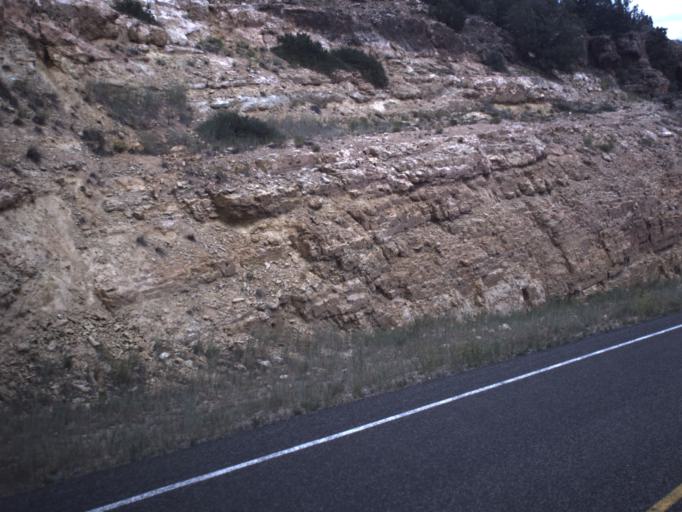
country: US
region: Utah
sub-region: Summit County
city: Francis
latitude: 40.4526
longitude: -110.8650
